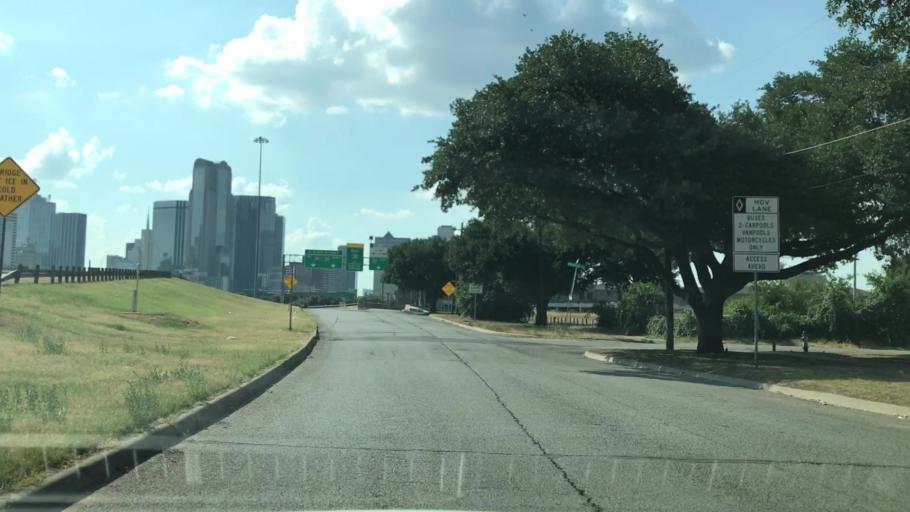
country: US
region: Texas
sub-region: Dallas County
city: Dallas
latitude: 32.7744
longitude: -96.7840
